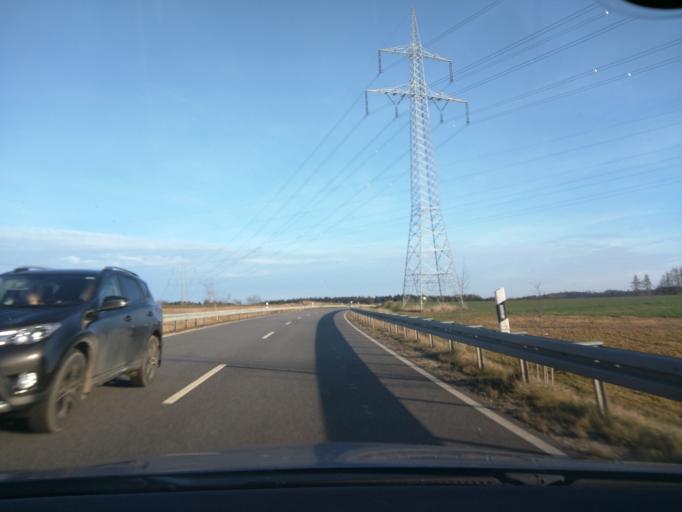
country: DE
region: Bavaria
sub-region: Upper Bavaria
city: Au in der Hallertau
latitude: 48.5605
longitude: 11.7283
